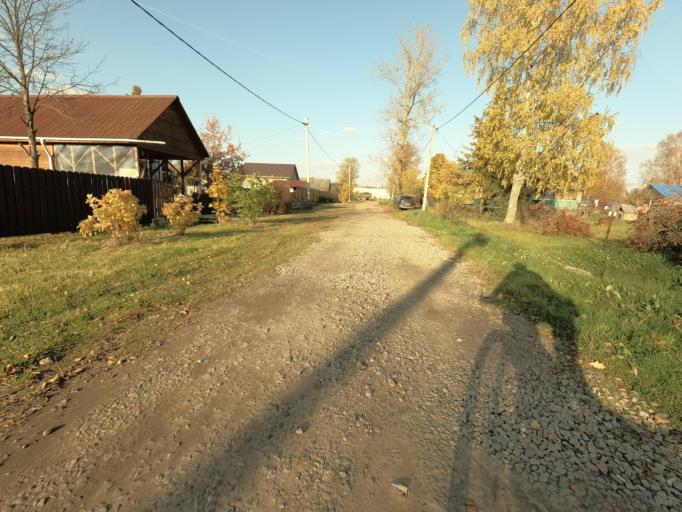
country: RU
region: Leningrad
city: Mga
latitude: 59.7545
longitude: 31.0510
